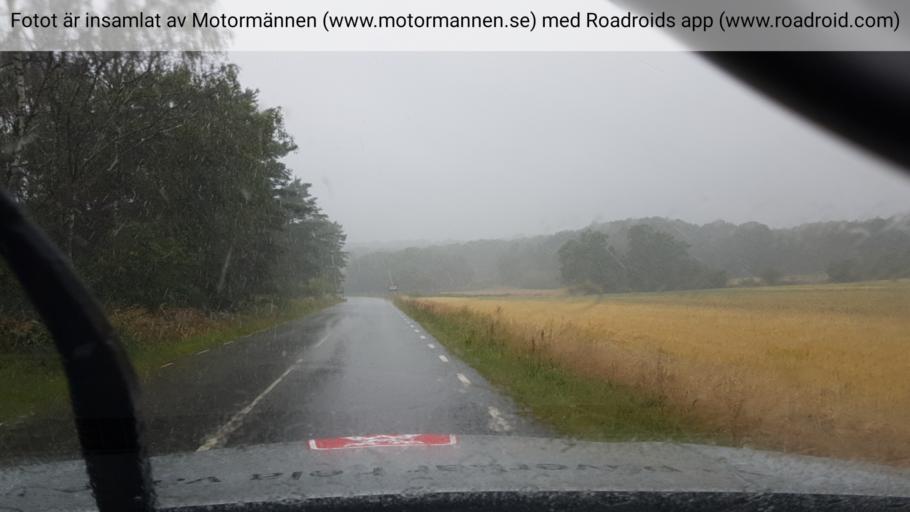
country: SE
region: Blekinge
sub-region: Solvesborgs Kommun
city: Soelvesborg
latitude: 56.0170
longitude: 14.7056
